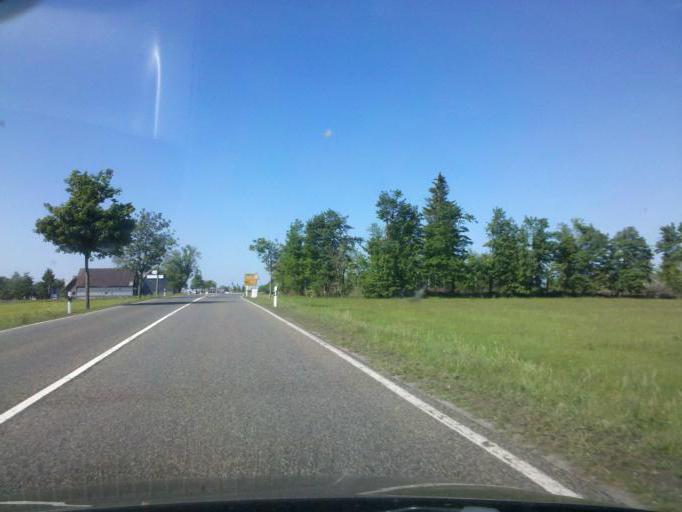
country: DE
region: Rheinland-Pfalz
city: Stein-Neukirch
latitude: 50.7023
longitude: 8.0667
